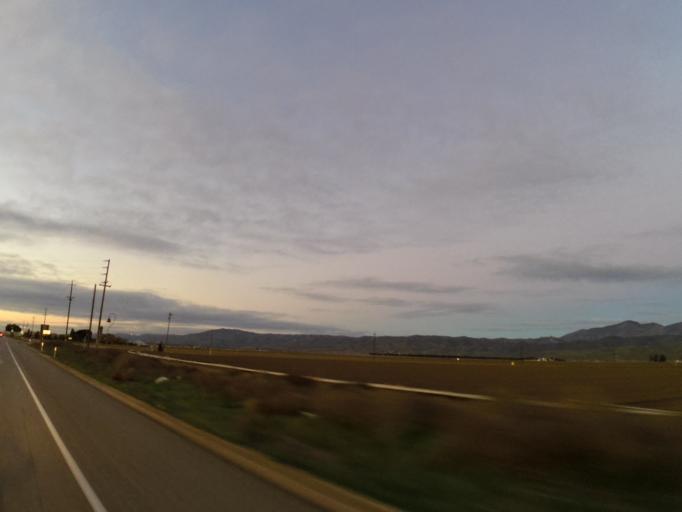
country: US
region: California
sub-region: Monterey County
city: Greenfield
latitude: 36.3516
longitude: -121.2665
